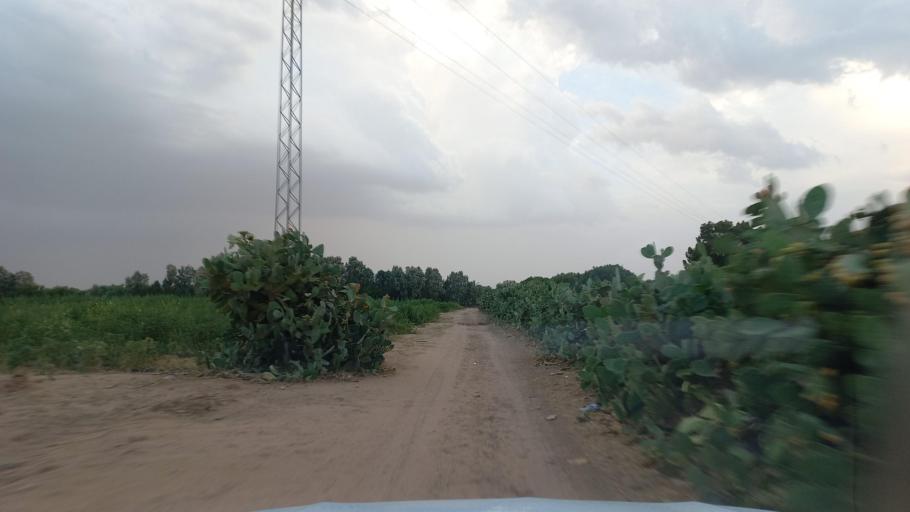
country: TN
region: Al Qasrayn
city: Kasserine
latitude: 35.2740
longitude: 9.0578
